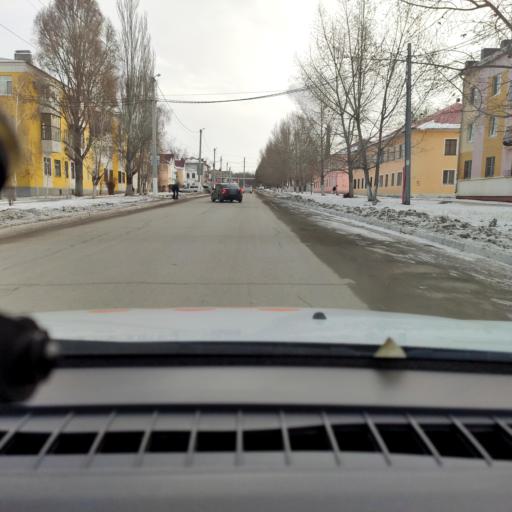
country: RU
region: Samara
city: Chapayevsk
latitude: 52.9731
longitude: 49.7023
